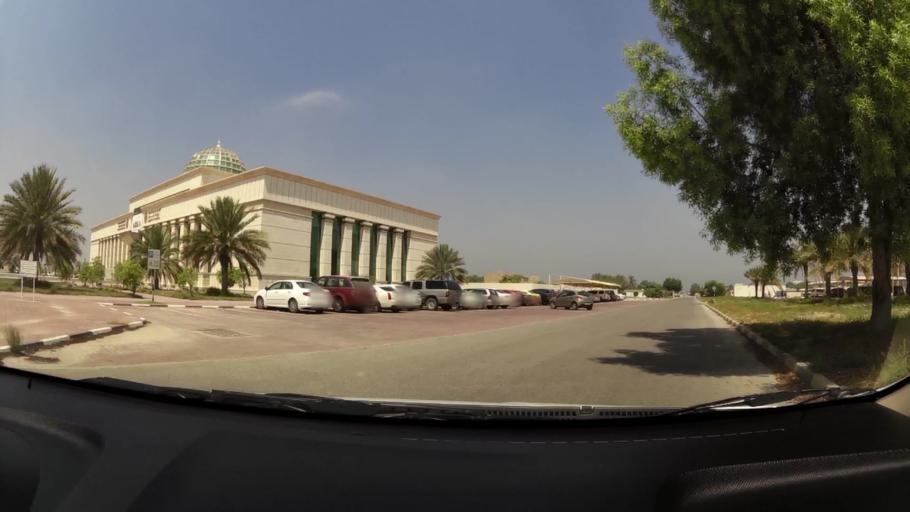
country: AE
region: Umm al Qaywayn
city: Umm al Qaywayn
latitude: 25.5706
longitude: 55.5640
